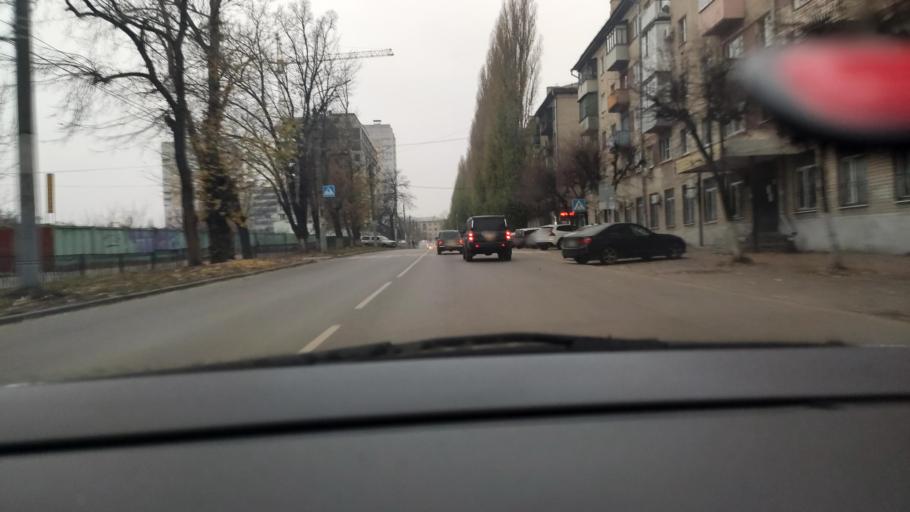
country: RU
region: Voronezj
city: Voronezh
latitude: 51.6794
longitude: 39.1911
